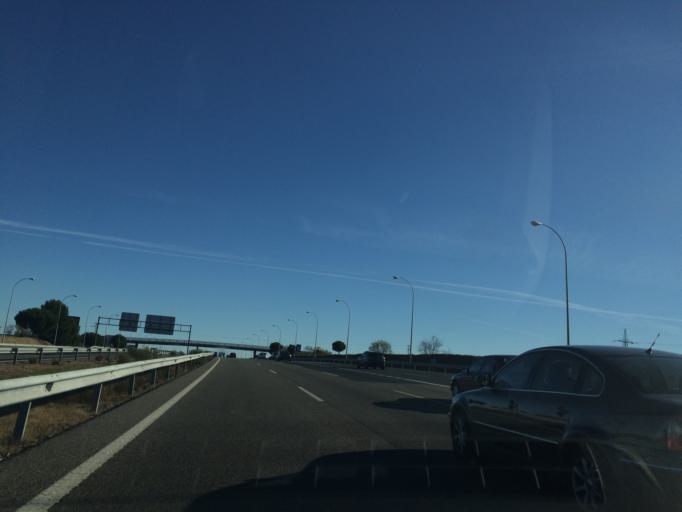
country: ES
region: Madrid
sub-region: Provincia de Madrid
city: Pozuelo de Alarcon
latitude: 40.4233
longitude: -3.8333
